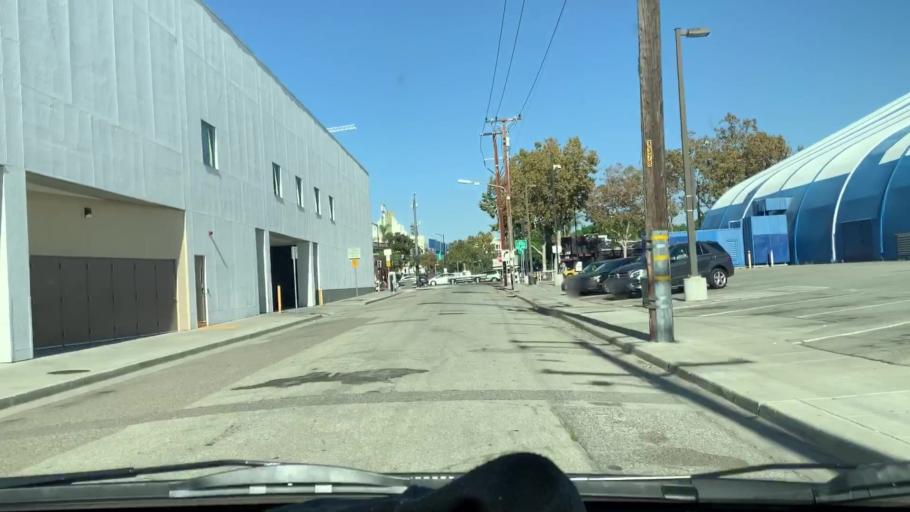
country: US
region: California
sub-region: Santa Clara County
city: San Jose
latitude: 37.3289
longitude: -121.8874
